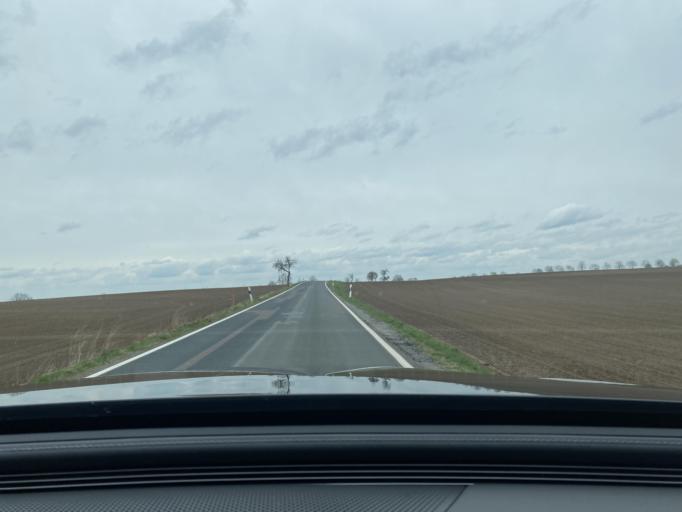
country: DE
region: Saxony
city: Goda
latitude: 51.1917
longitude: 14.3239
